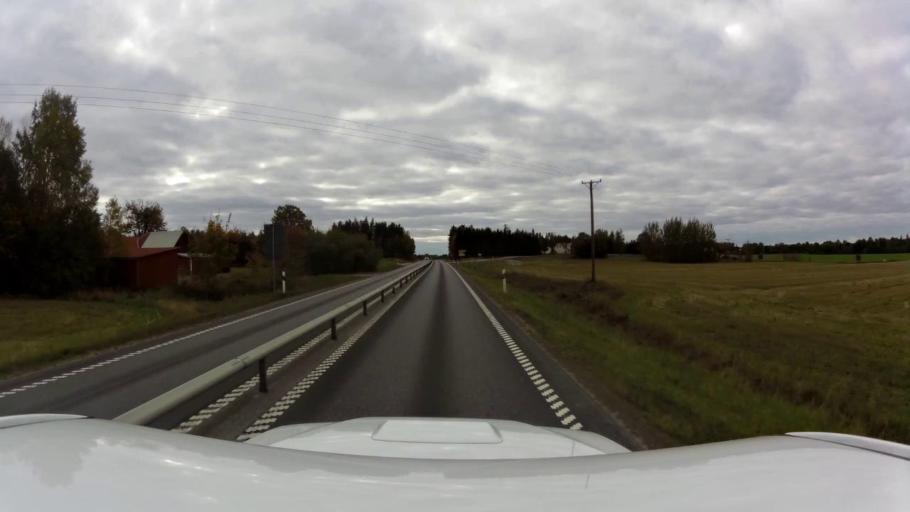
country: SE
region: OEstergoetland
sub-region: Linkopings Kommun
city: Malmslatt
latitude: 58.3595
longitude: 15.5455
